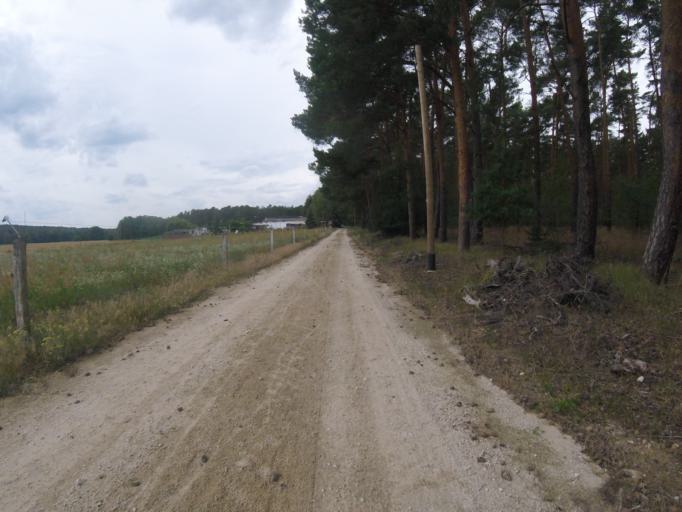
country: DE
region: Brandenburg
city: Bestensee
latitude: 52.2575
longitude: 13.7036
